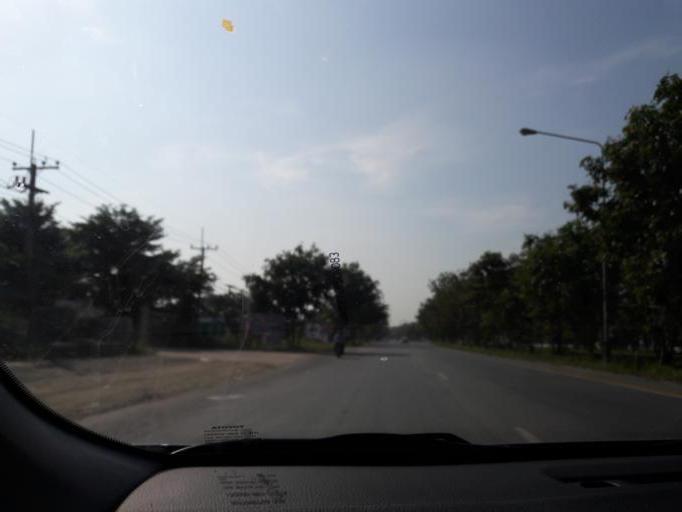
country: TH
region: Ang Thong
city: Ang Thong
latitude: 14.5809
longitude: 100.4427
